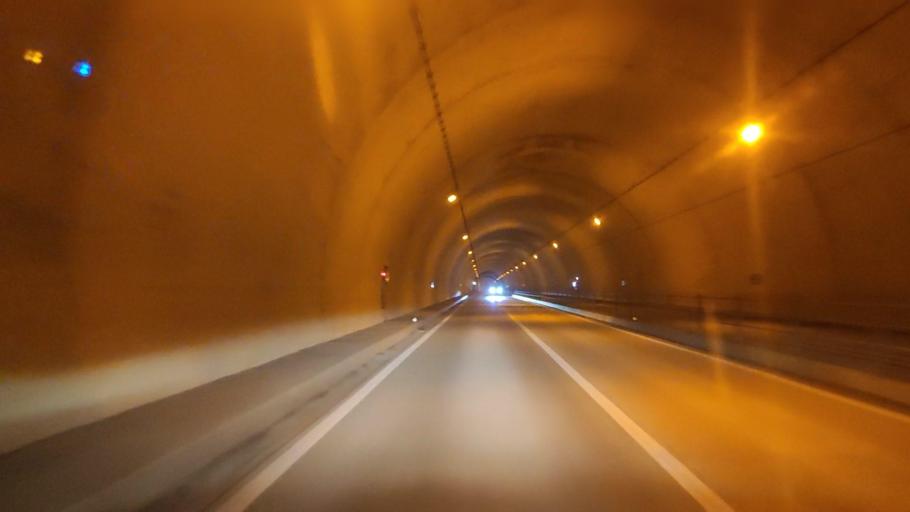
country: JP
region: Kumamoto
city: Hitoyoshi
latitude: 32.3923
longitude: 130.8283
